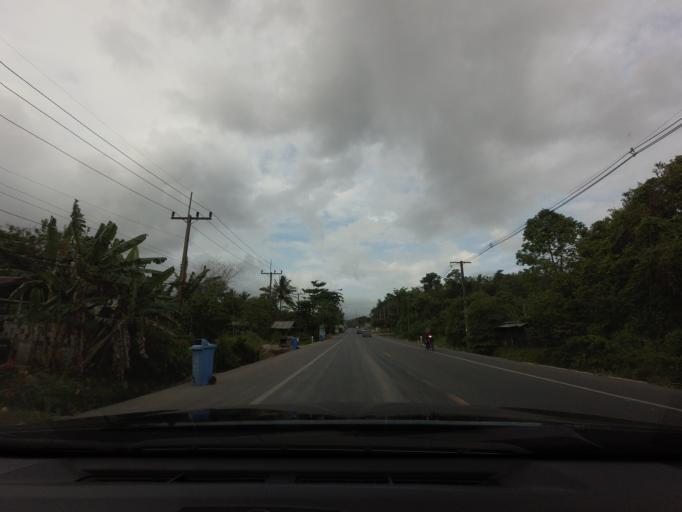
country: TH
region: Yala
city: Raman
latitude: 6.4710
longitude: 101.3957
